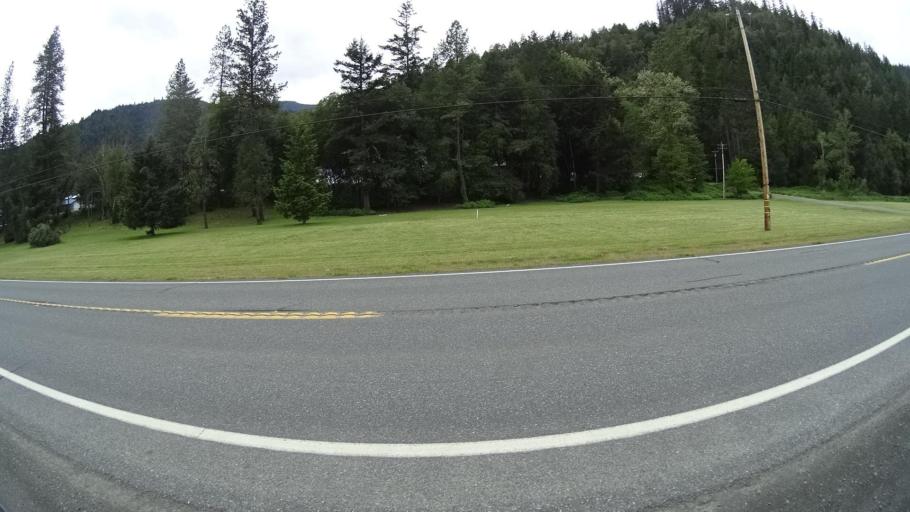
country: US
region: California
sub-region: Humboldt County
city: Willow Creek
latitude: 40.9503
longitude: -123.6386
